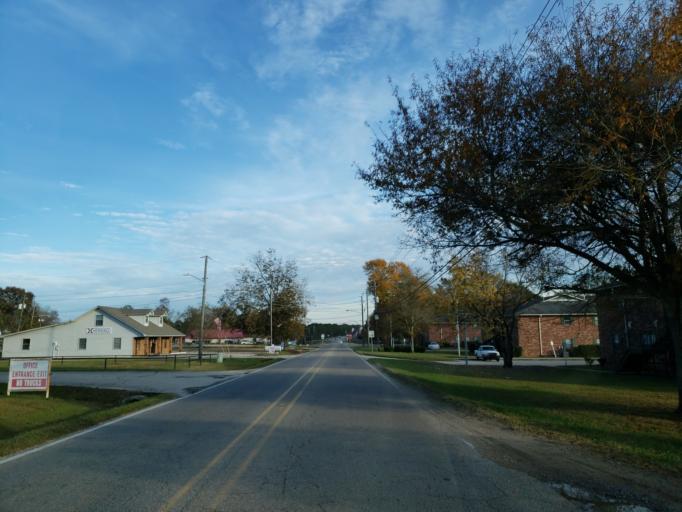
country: US
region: Mississippi
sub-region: Lamar County
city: Purvis
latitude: 31.1539
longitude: -89.4136
